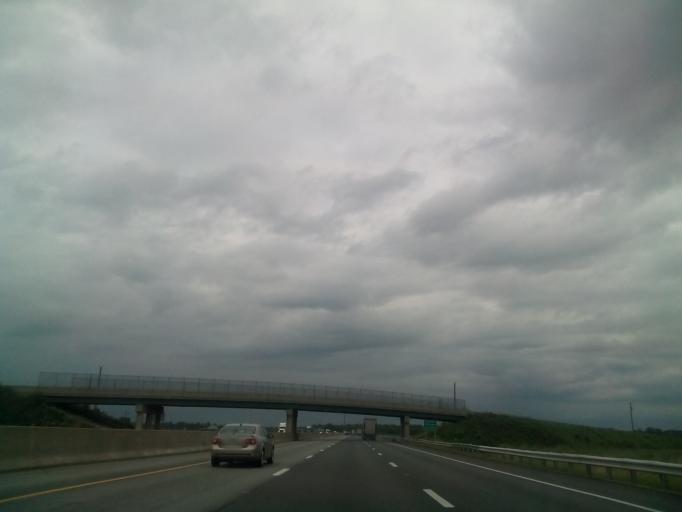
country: US
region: Ohio
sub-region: Sandusky County
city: Woodville
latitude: 41.4771
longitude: -83.3399
